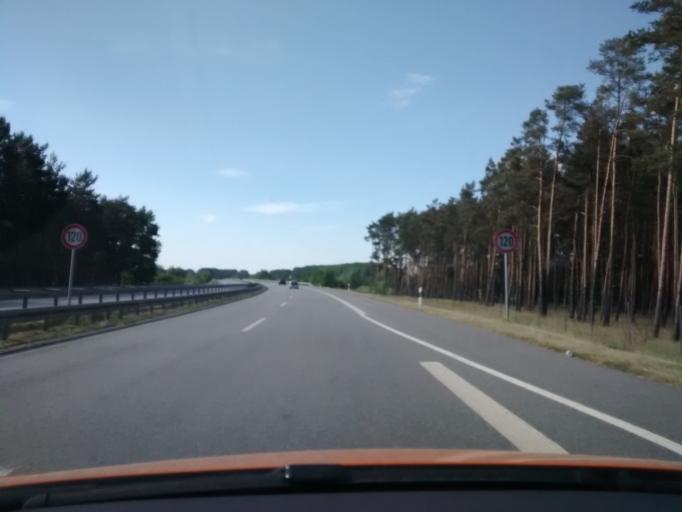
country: DE
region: Brandenburg
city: Trebbin
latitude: 52.2144
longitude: 13.2581
